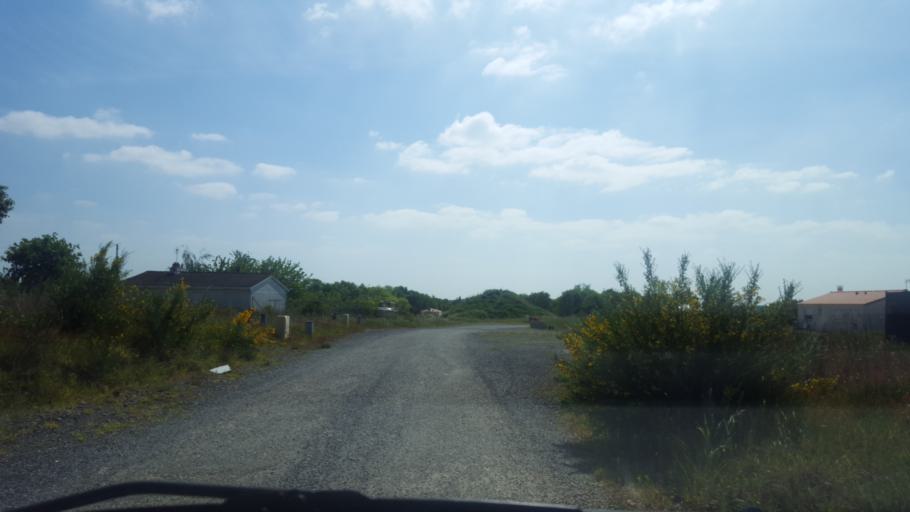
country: FR
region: Pays de la Loire
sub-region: Departement de la Loire-Atlantique
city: La Limouziniere
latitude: 46.9612
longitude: -1.5765
